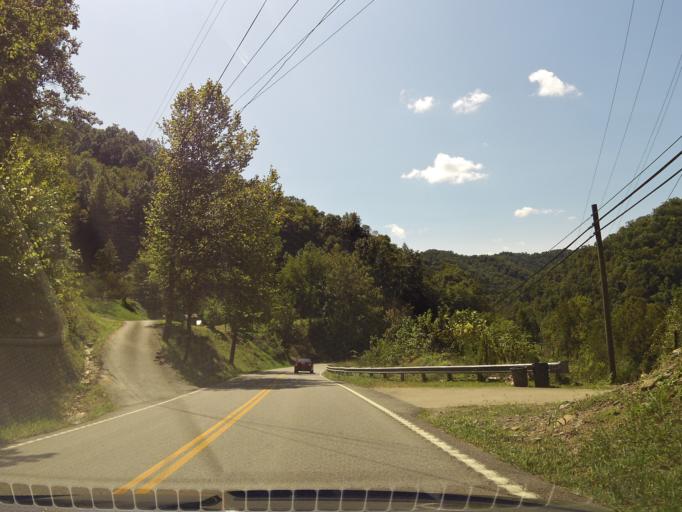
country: US
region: Kentucky
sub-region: Leslie County
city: Hyden
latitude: 37.0984
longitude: -83.3965
